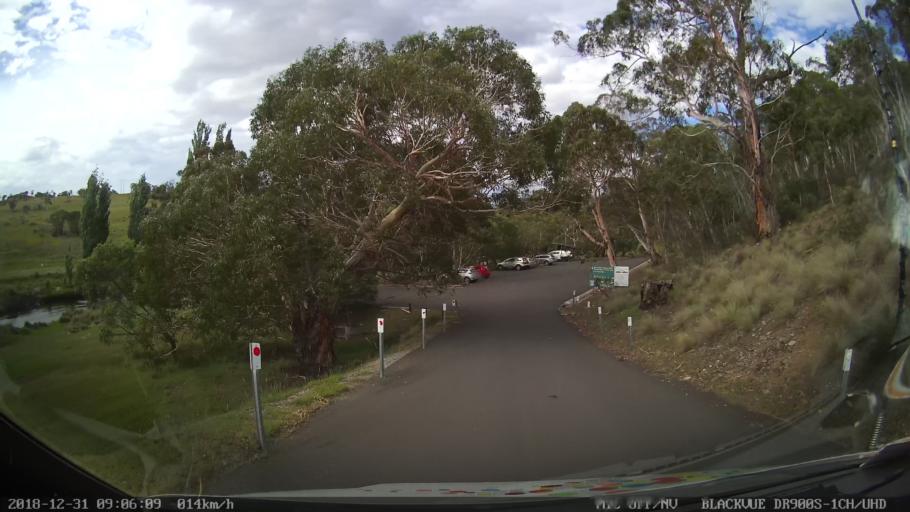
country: AU
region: New South Wales
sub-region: Snowy River
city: Jindabyne
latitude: -36.3689
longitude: 148.5895
